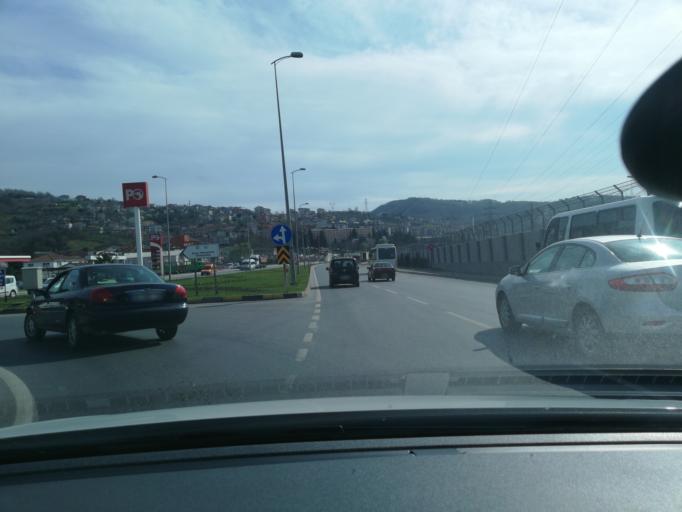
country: TR
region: Zonguldak
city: Eregli
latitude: 41.2608
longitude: 31.4351
